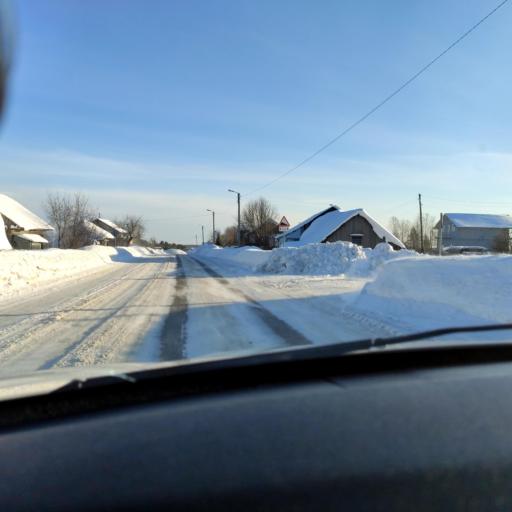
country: RU
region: Perm
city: Polazna
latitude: 58.3182
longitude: 56.4308
